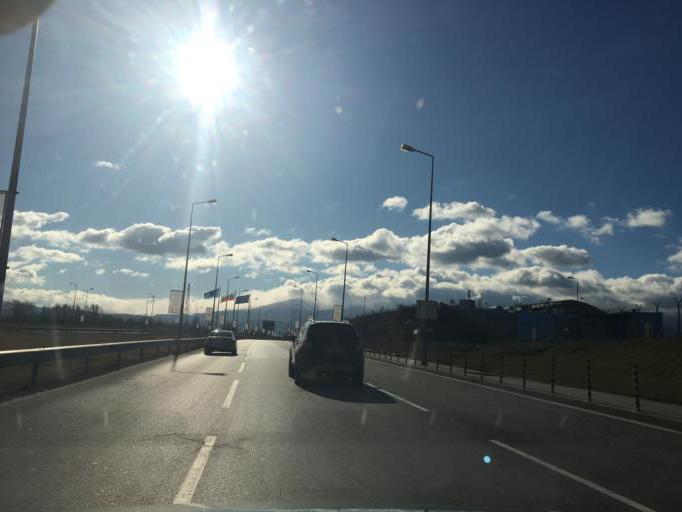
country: BG
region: Sofia-Capital
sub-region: Stolichna Obshtina
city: Sofia
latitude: 42.6870
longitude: 23.4127
